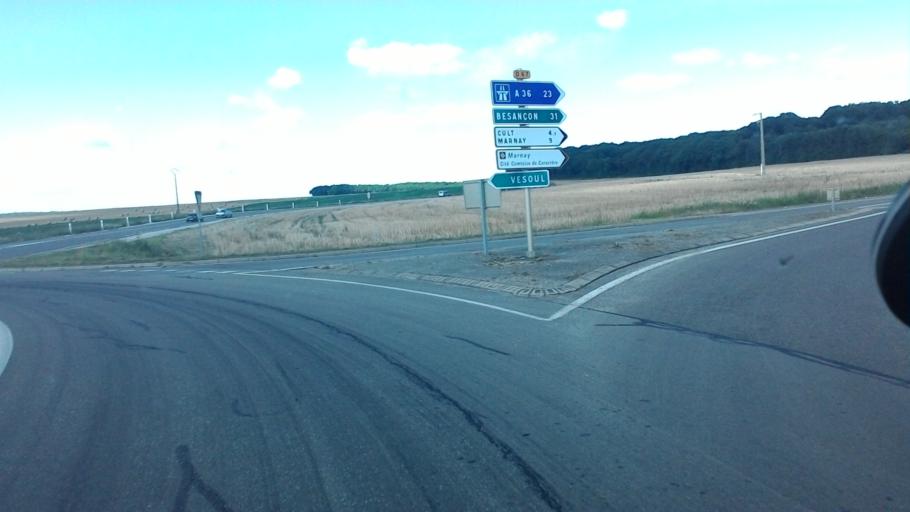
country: FR
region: Franche-Comte
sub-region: Departement de la Haute-Saone
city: Marnay
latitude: 47.3413
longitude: 5.7018
